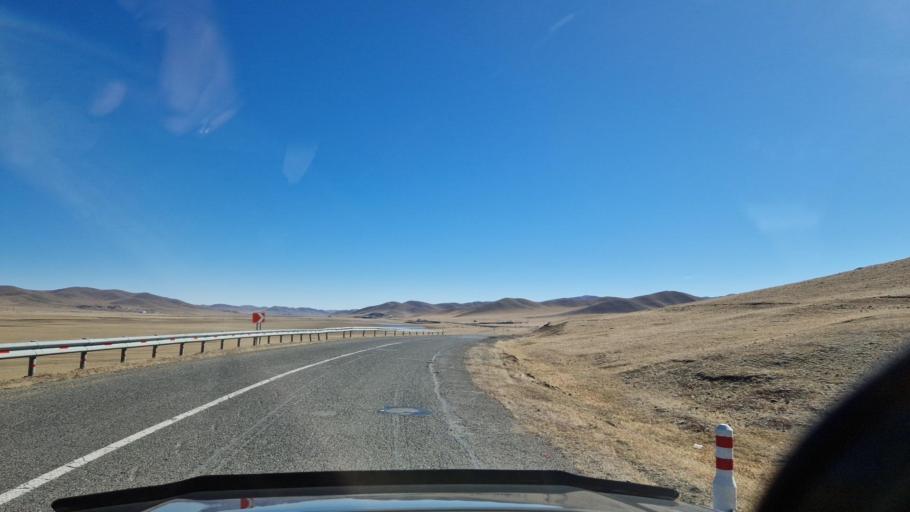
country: MN
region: Hentiy
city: Modot
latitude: 47.7435
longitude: 108.9942
